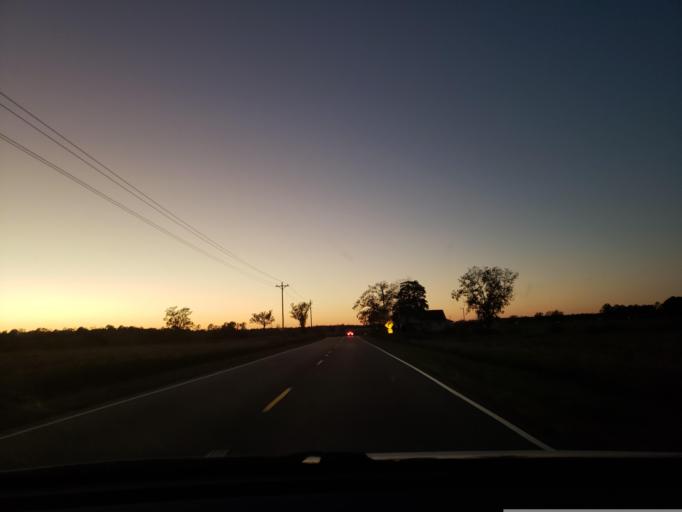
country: US
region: North Carolina
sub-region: Duplin County
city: Kenansville
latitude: 34.8876
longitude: -77.9015
